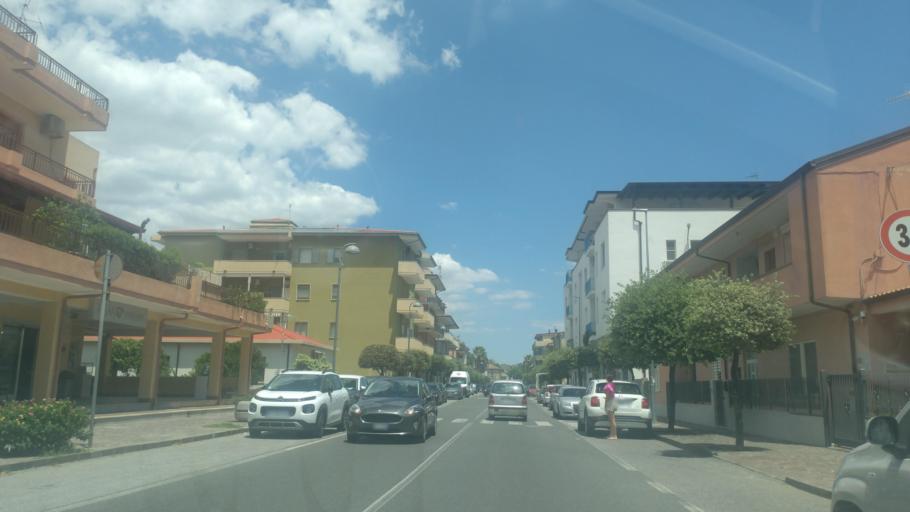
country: IT
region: Calabria
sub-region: Provincia di Catanzaro
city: Montepaone Lido
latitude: 38.7270
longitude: 16.5399
